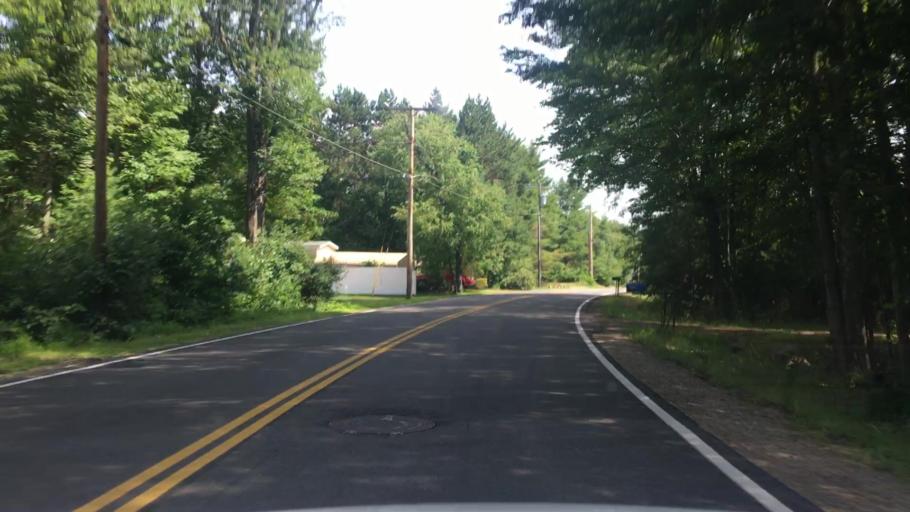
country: US
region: New Hampshire
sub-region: Strafford County
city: Rochester
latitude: 43.3379
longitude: -70.9596
